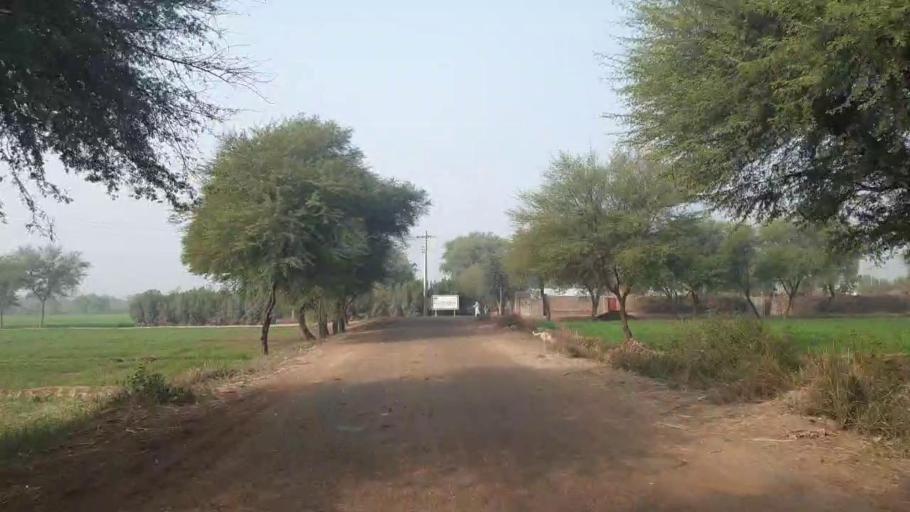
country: PK
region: Sindh
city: Tando Adam
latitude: 25.8042
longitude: 68.6140
